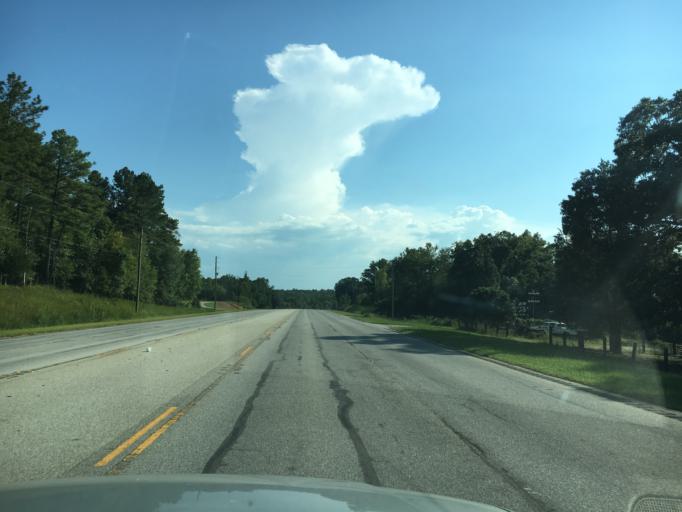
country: US
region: South Carolina
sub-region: Laurens County
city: Clinton
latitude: 34.4114
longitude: -81.9252
